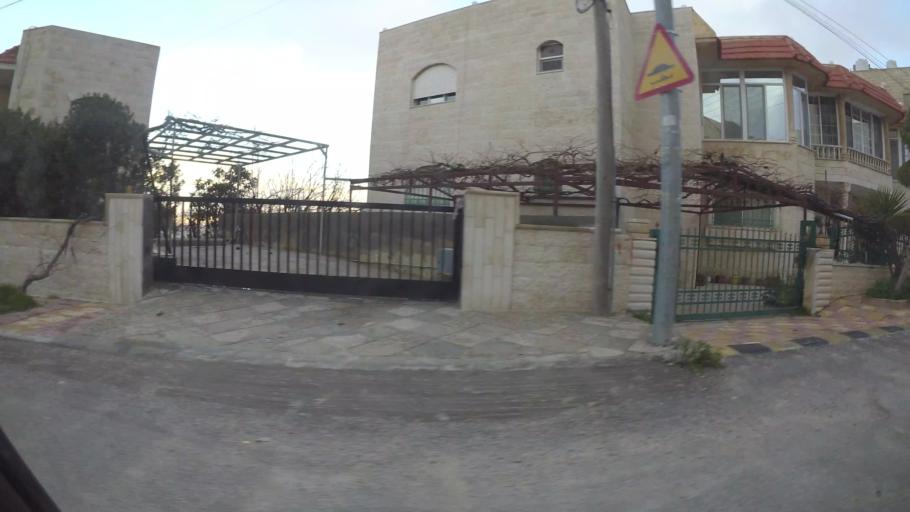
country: JO
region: Amman
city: Al Jubayhah
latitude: 32.0492
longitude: 35.8964
